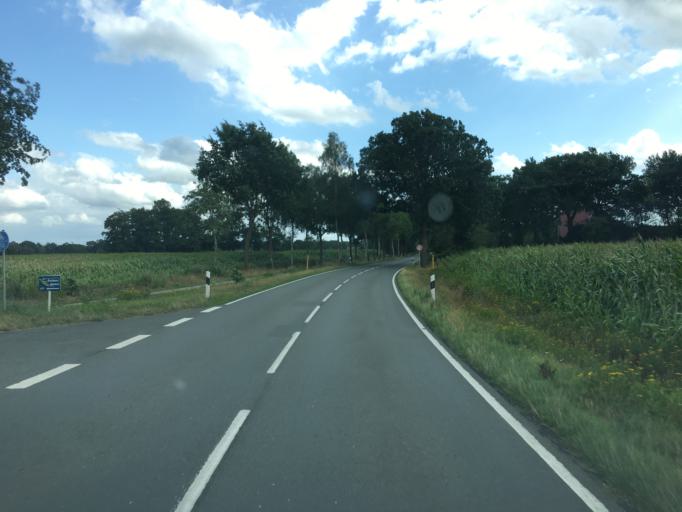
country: DE
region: Lower Saxony
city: Friesoythe
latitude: 53.0554
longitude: 7.8566
